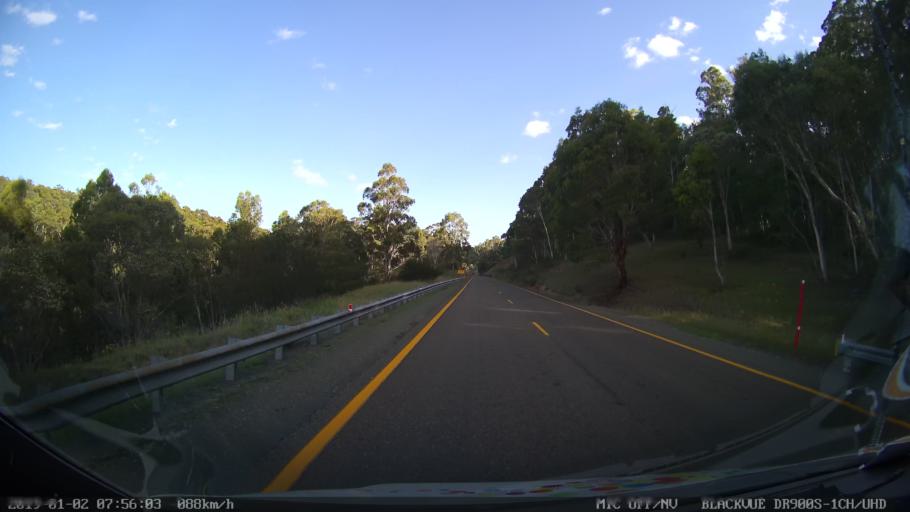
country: AU
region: New South Wales
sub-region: Tumut Shire
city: Tumut
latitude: -35.6755
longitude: 148.4861
